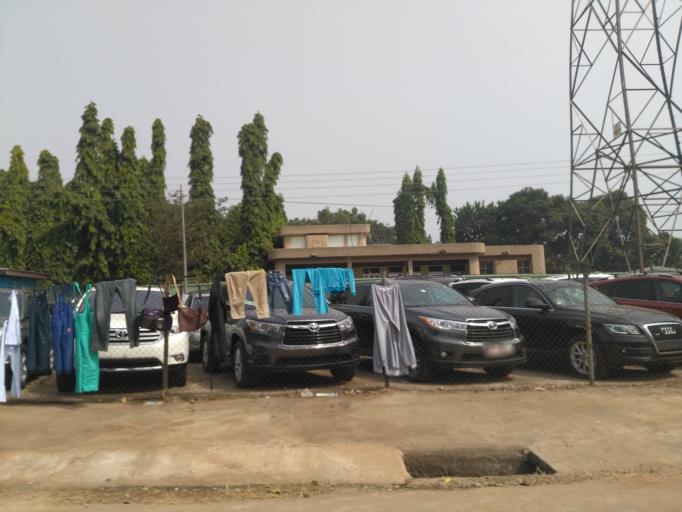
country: GH
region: Ashanti
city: Kumasi
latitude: 6.6713
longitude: -1.6379
